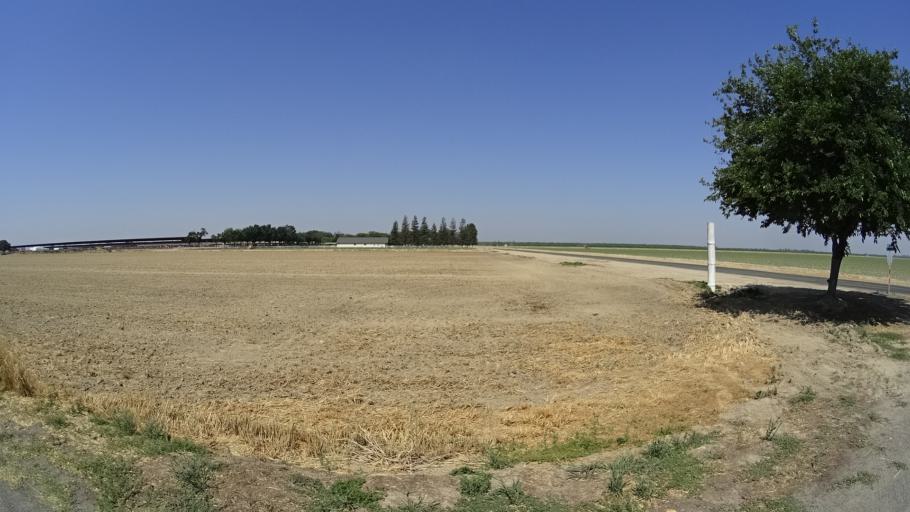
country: US
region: California
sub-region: Fresno County
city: Kingsburg
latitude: 36.4158
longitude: -119.5287
